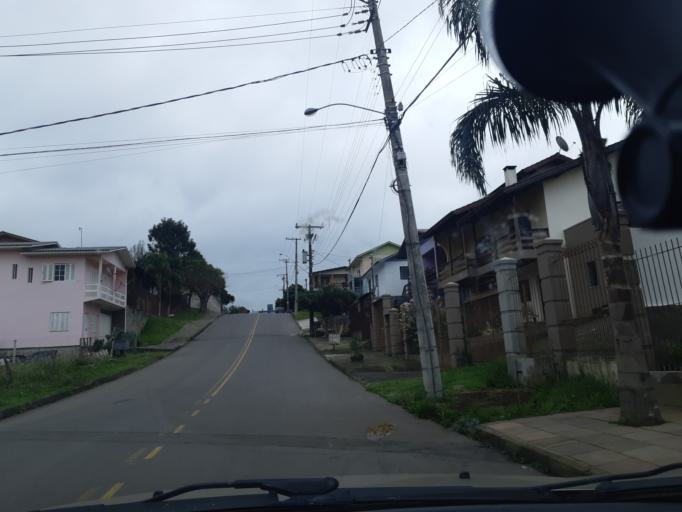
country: BR
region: Rio Grande do Sul
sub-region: Caxias Do Sul
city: Caxias do Sul
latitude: -29.1589
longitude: -51.2072
